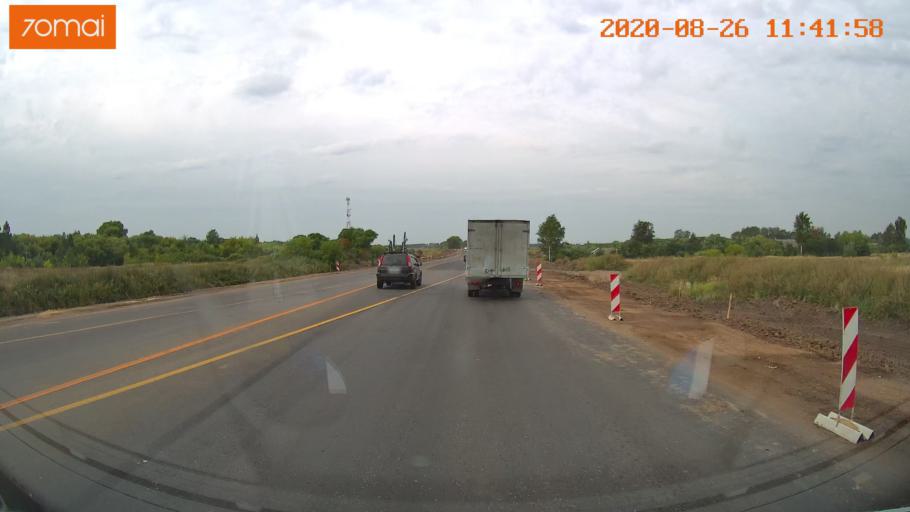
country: RU
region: Rjazan
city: Shilovo
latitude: 54.2961
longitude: 40.7011
